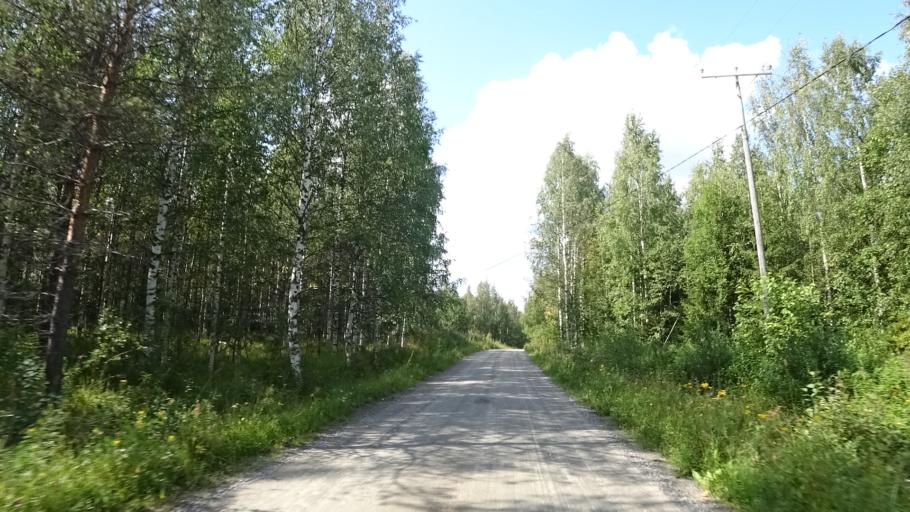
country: FI
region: North Karelia
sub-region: Joensuu
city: Ilomantsi
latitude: 62.9312
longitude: 31.3105
